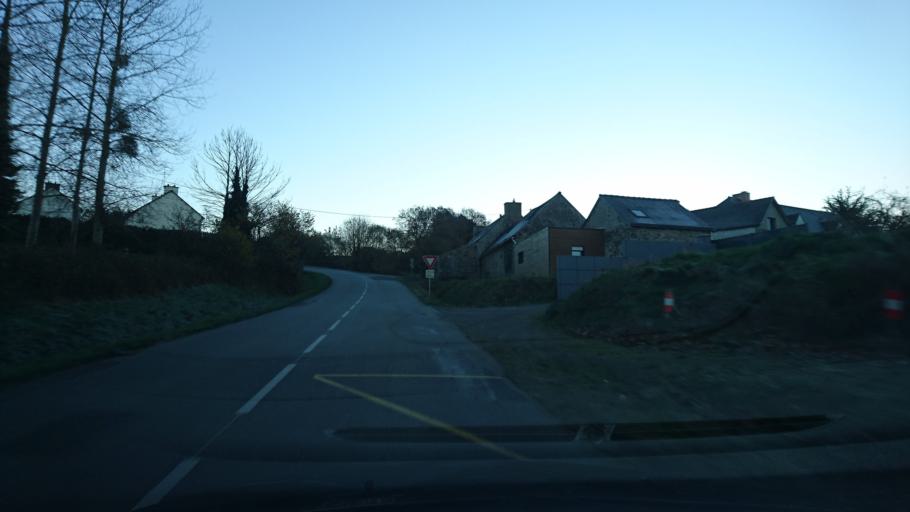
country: FR
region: Brittany
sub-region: Departement des Cotes-d'Armor
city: Pledran
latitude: 48.4582
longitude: -2.7578
